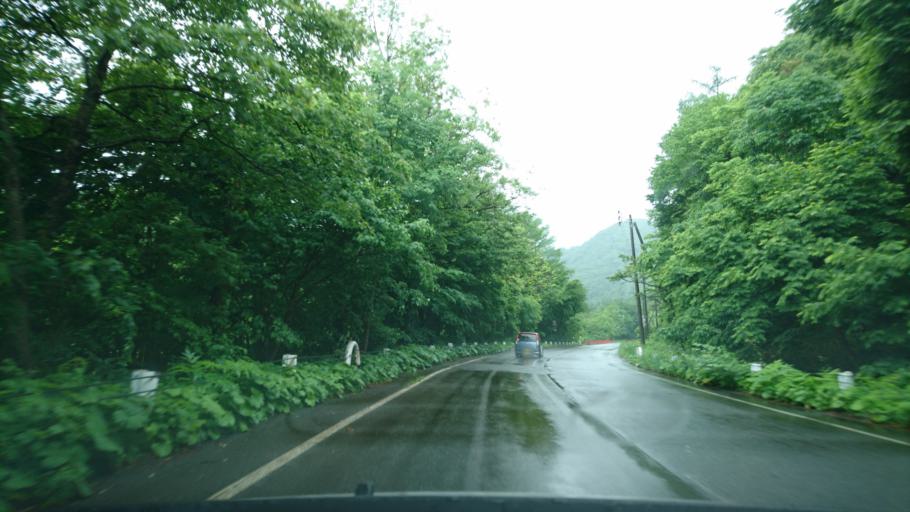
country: JP
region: Iwate
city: Ichinoseki
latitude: 39.0051
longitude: 140.8618
